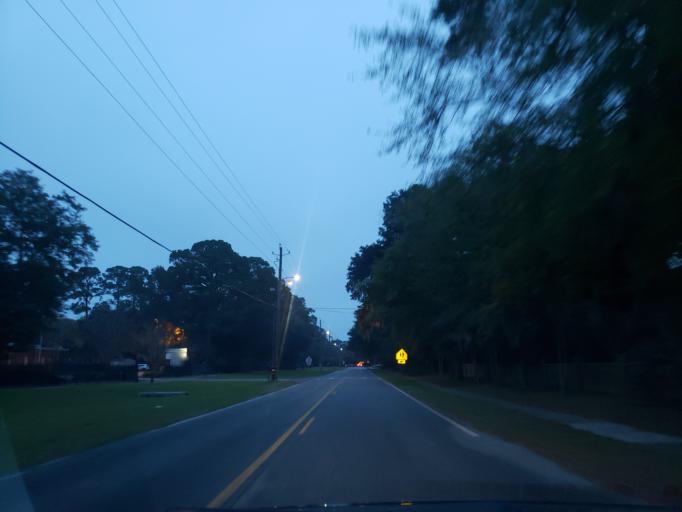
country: US
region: Georgia
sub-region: Chatham County
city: Wilmington Island
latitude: 32.0201
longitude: -80.9670
